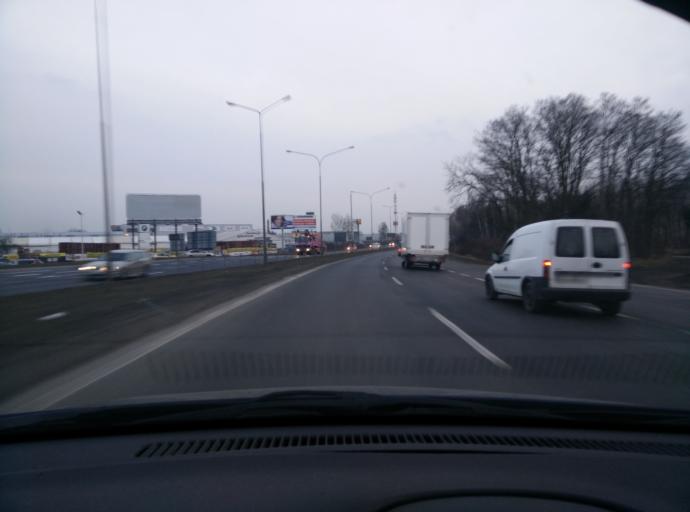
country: PL
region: Greater Poland Voivodeship
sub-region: Poznan
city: Poznan
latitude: 52.3686
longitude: 16.9910
